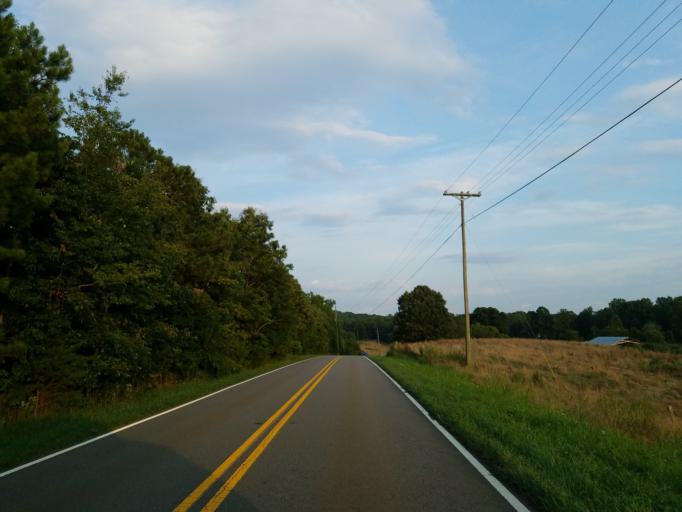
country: US
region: Georgia
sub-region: Pickens County
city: Jasper
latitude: 34.5598
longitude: -84.4723
